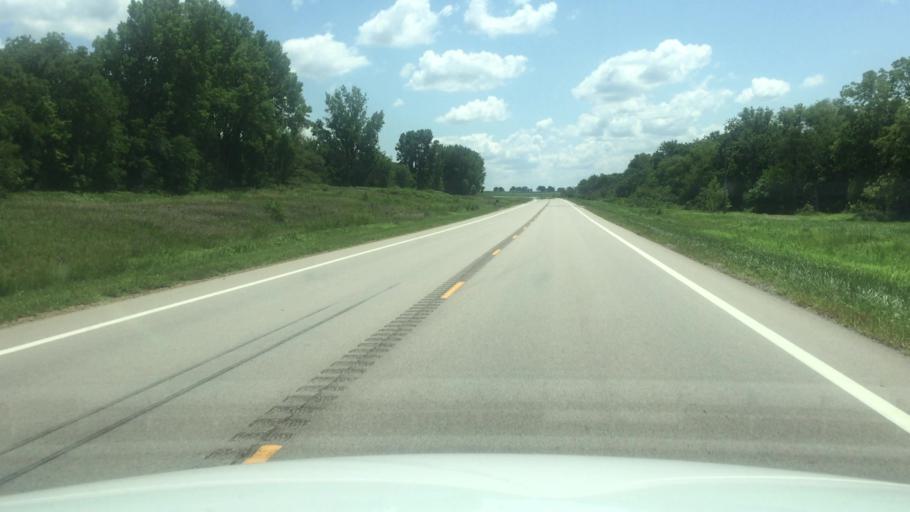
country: US
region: Kansas
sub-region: Brown County
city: Horton
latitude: 39.6213
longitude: -95.3495
